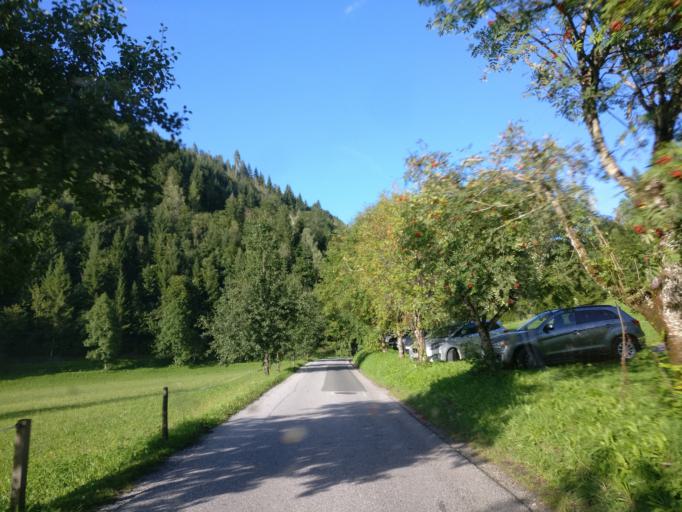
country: AT
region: Salzburg
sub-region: Politischer Bezirk Zell am See
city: Lend
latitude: 47.3138
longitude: 13.0447
